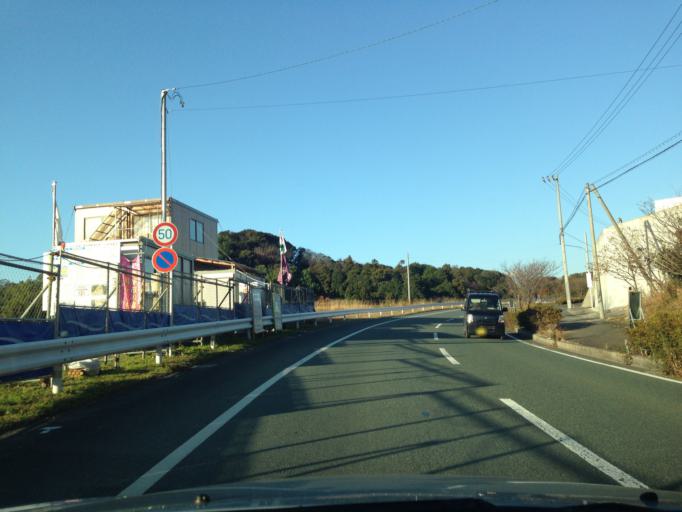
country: JP
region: Shizuoka
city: Fukuroi
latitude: 34.7370
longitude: 137.9634
